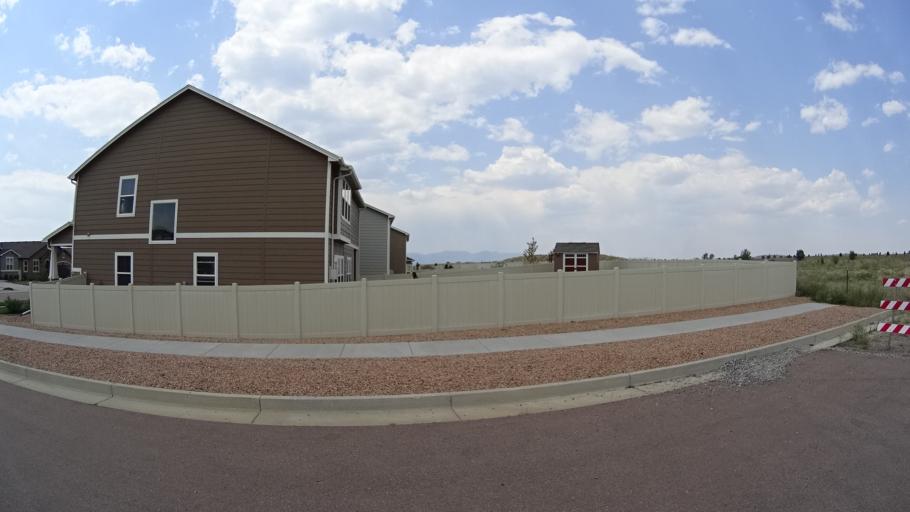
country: US
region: Colorado
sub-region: El Paso County
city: Black Forest
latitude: 38.9547
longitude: -104.6920
